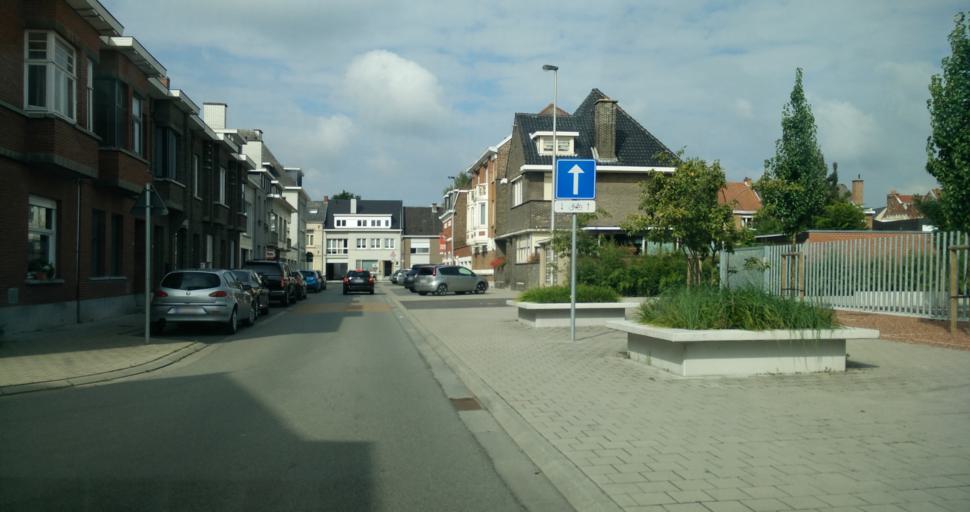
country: BE
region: Flanders
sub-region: Provincie Oost-Vlaanderen
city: Oudenaarde
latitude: 50.8473
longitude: 3.6126
